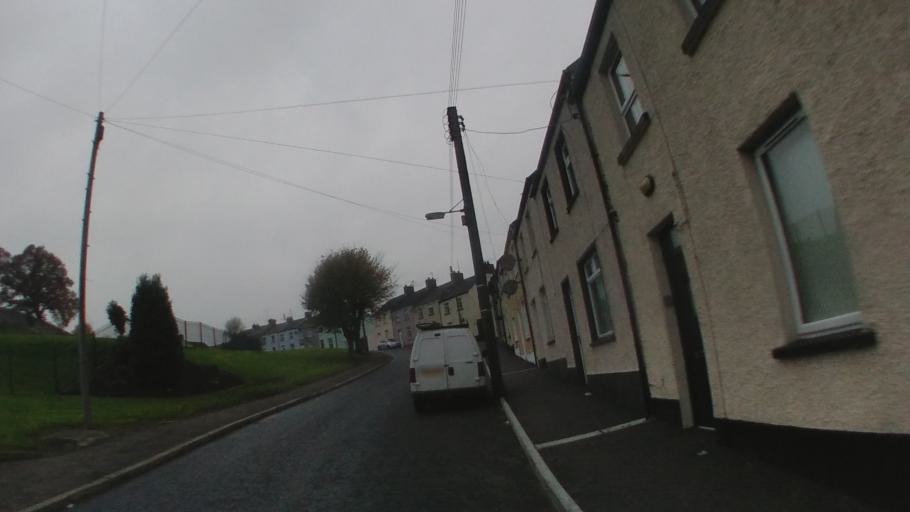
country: GB
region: Northern Ireland
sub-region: Newry and Mourne District
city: Newry
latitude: 54.1786
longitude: -6.3308
